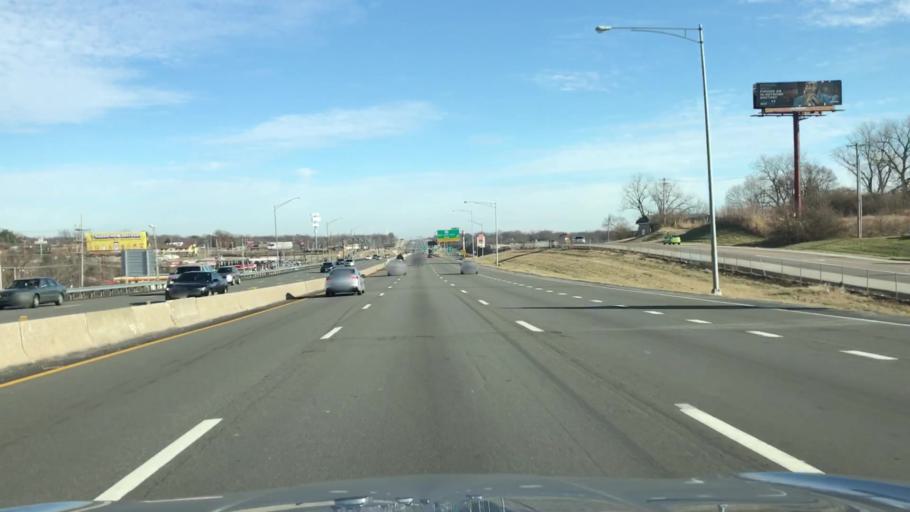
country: US
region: Missouri
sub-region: Saint Louis County
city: Black Jack
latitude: 38.7710
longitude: -90.2728
